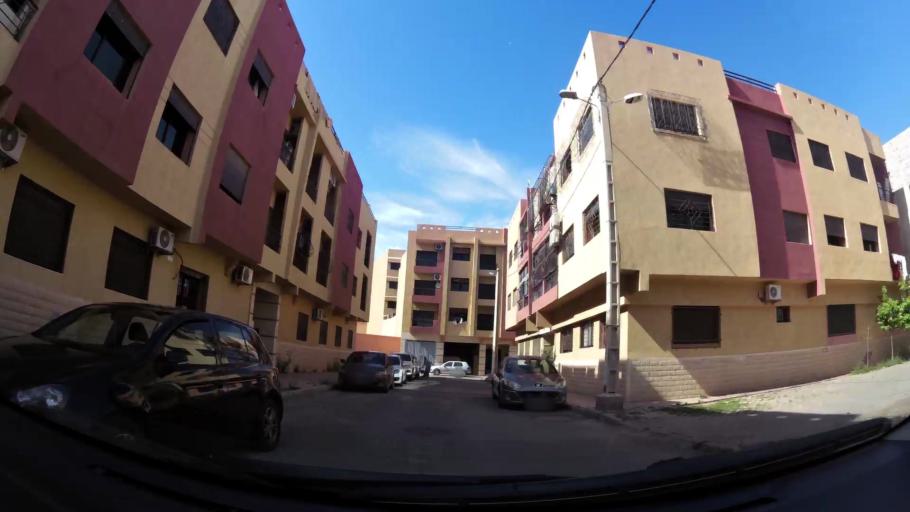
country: MA
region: Marrakech-Tensift-Al Haouz
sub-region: Marrakech
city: Marrakesh
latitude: 31.6448
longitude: -7.9792
